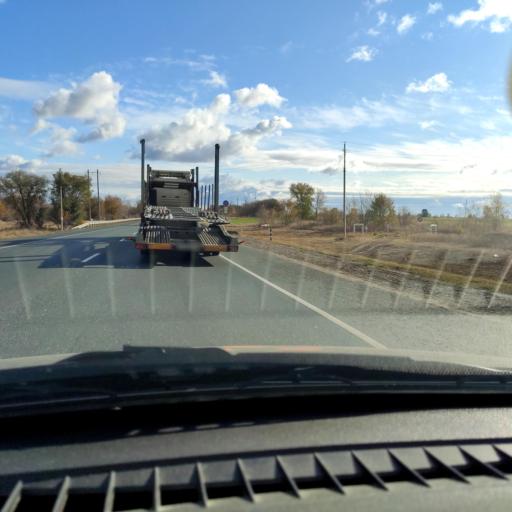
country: RU
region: Samara
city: Varlamovo
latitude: 53.1961
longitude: 48.3142
